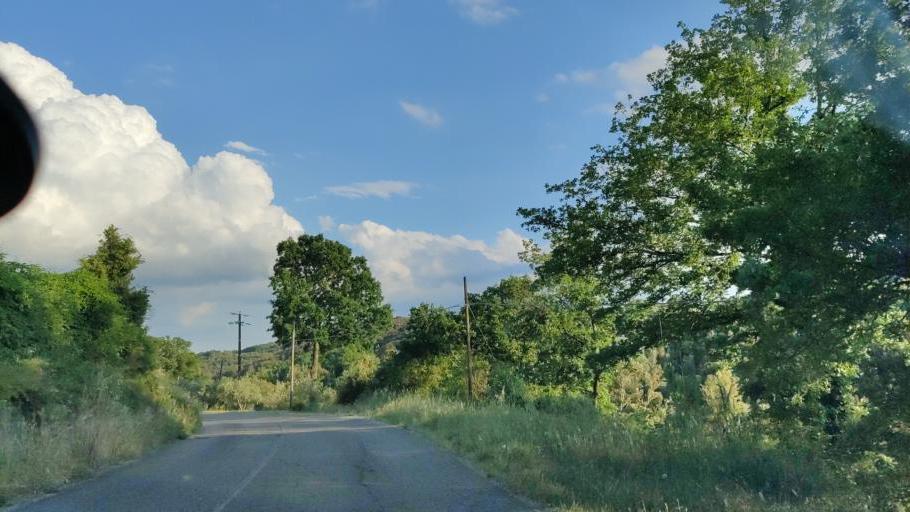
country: IT
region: Umbria
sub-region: Provincia di Terni
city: Amelia
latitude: 42.5786
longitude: 12.3928
